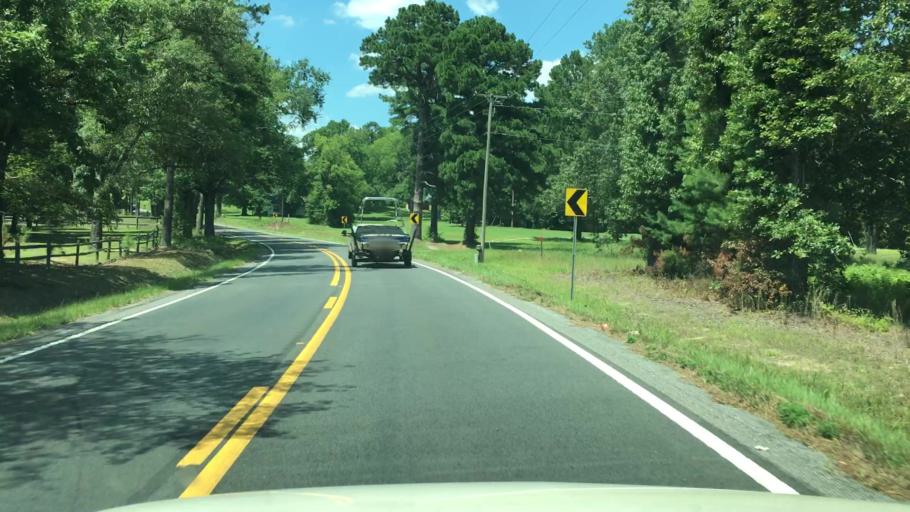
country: US
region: Arkansas
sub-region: Clark County
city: Arkadelphia
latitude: 34.2618
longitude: -93.1300
